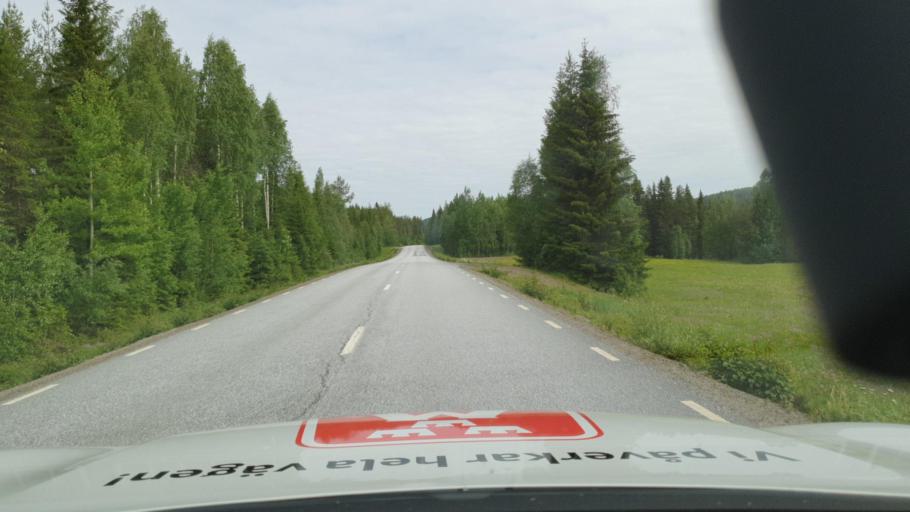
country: SE
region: Vaesterbotten
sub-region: Umea Kommun
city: Ersmark
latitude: 64.2879
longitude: 20.2222
